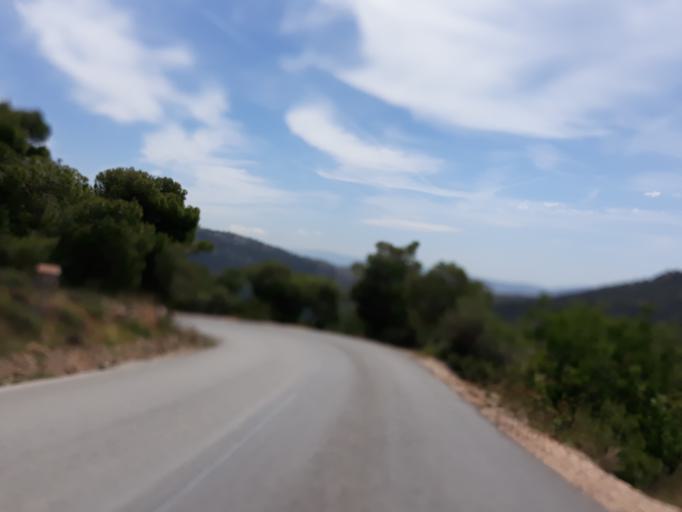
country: GR
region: Attica
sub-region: Nomarchia Dytikis Attikis
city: Magoula
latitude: 38.1478
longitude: 23.5176
